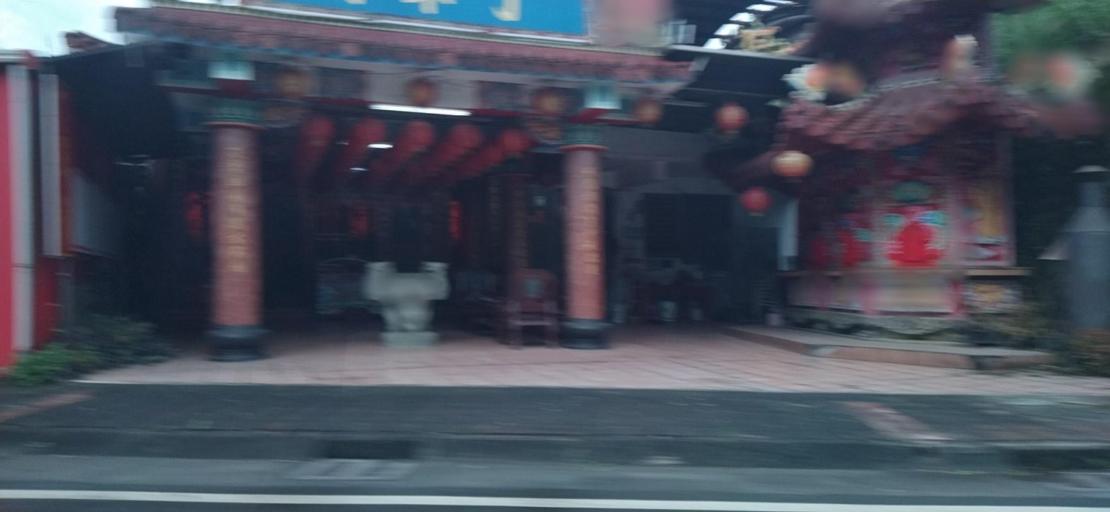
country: TW
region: Taiwan
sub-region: Yilan
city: Yilan
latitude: 24.6067
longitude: 121.8371
